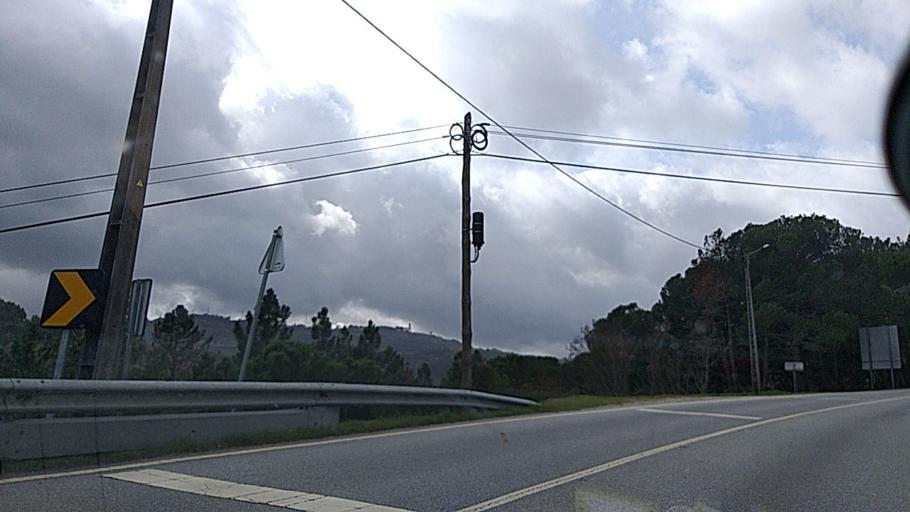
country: PT
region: Viseu
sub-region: Mangualde
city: Mangualde
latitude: 40.6335
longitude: -7.7398
